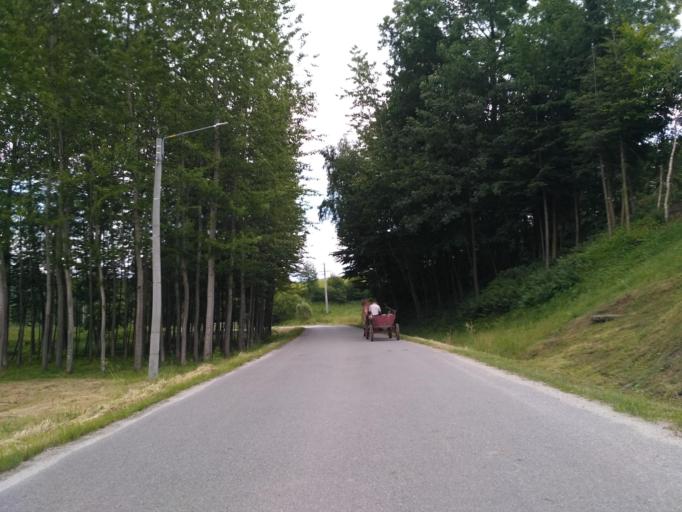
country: PL
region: Subcarpathian Voivodeship
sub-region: Powiat przeworski
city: Jawornik Polski
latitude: 49.8507
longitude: 22.2924
